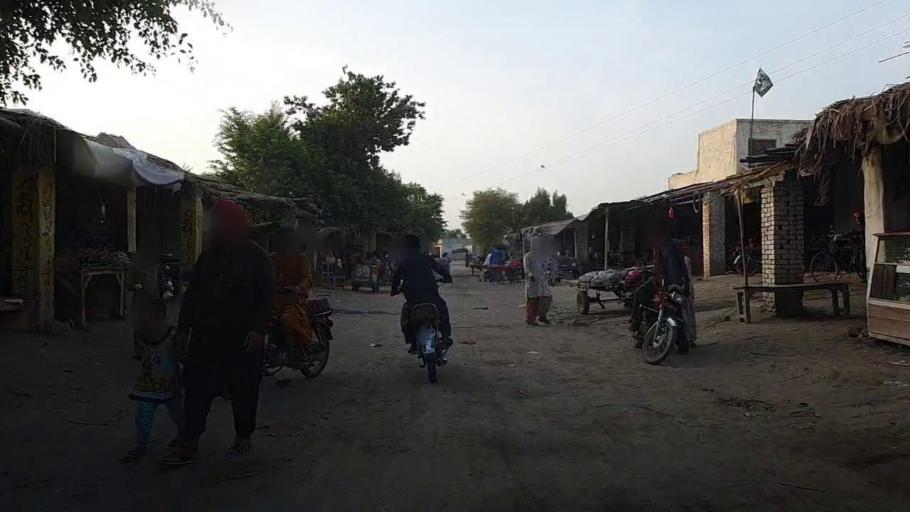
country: PK
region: Sindh
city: Ubauro
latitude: 28.2188
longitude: 69.8212
